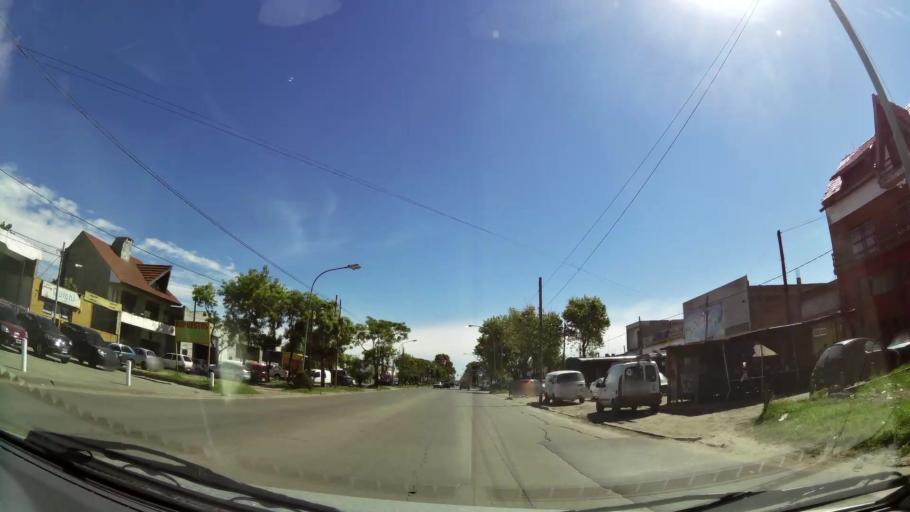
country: AR
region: Buenos Aires
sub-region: Partido de Almirante Brown
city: Adrogue
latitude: -34.7578
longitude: -58.3542
